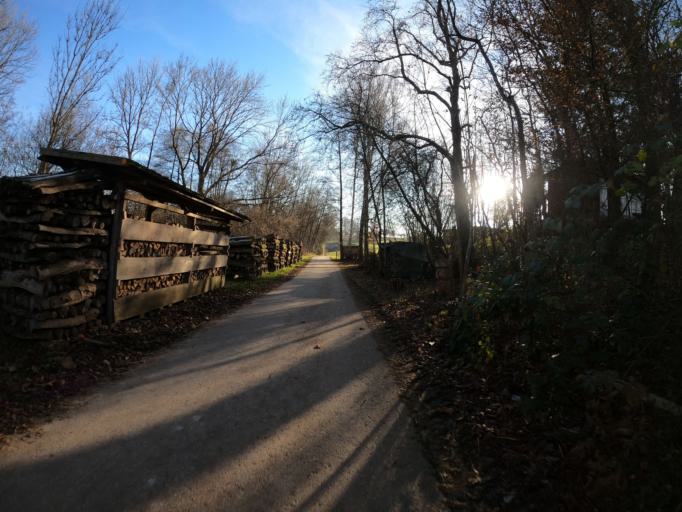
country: DE
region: Baden-Wuerttemberg
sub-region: Regierungsbezirk Stuttgart
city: Goeppingen
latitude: 48.6891
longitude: 9.6232
